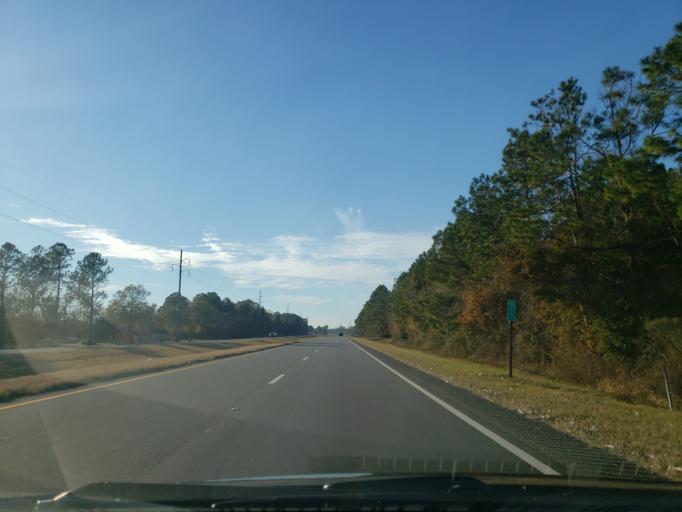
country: US
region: Georgia
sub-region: Atkinson County
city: Pearson
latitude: 31.2942
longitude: -82.8292
